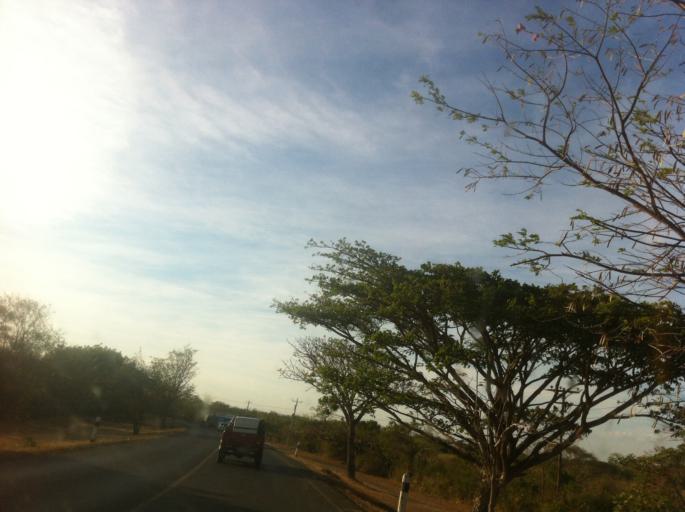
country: NI
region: Rivas
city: Rivas
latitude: 11.4012
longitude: -85.7815
